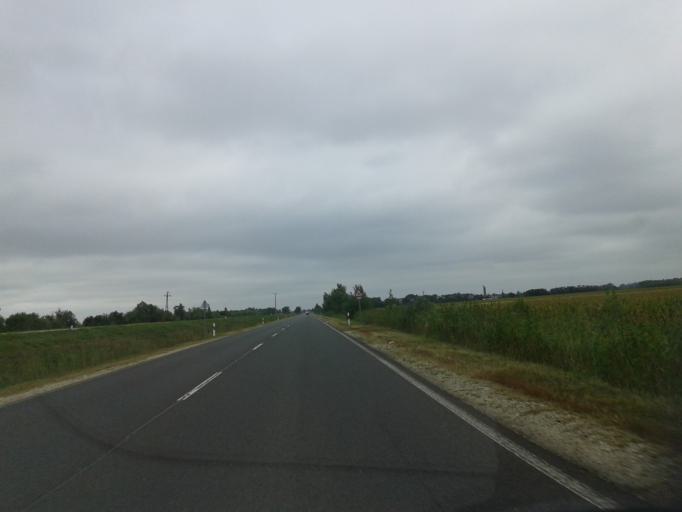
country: HU
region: Bacs-Kiskun
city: Solt
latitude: 46.7726
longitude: 19.0071
